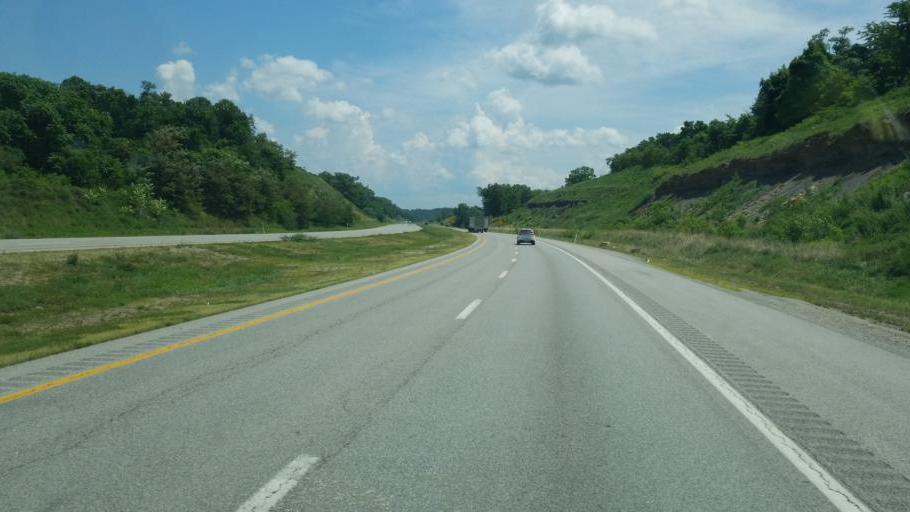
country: US
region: West Virginia
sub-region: Mason County
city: Point Pleasant
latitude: 38.7892
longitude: -82.0921
